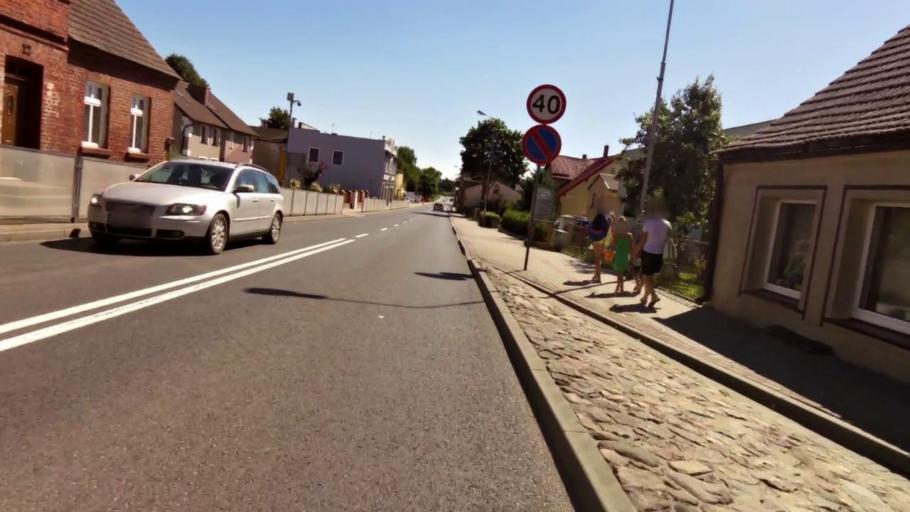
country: PL
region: West Pomeranian Voivodeship
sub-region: Powiat szczecinecki
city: Bialy Bor
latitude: 53.8992
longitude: 16.8339
